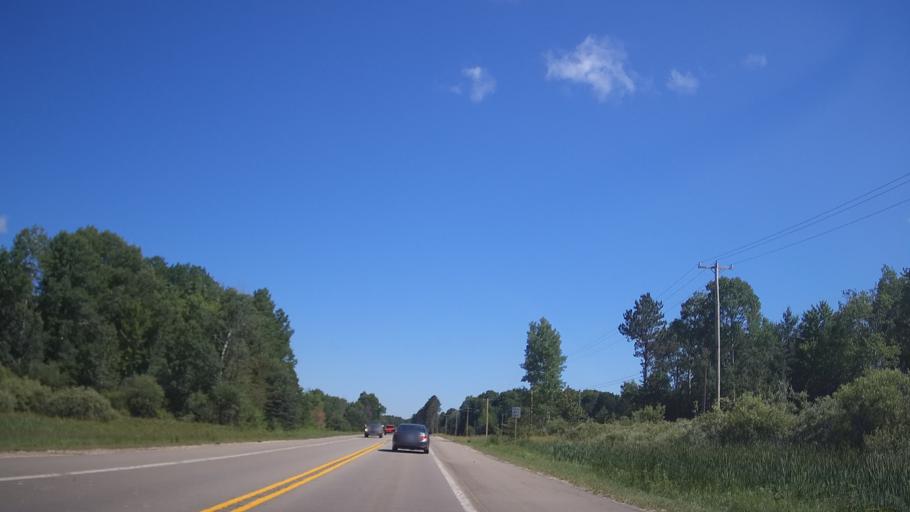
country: US
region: Michigan
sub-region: Cheboygan County
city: Indian River
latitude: 45.5307
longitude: -84.7819
